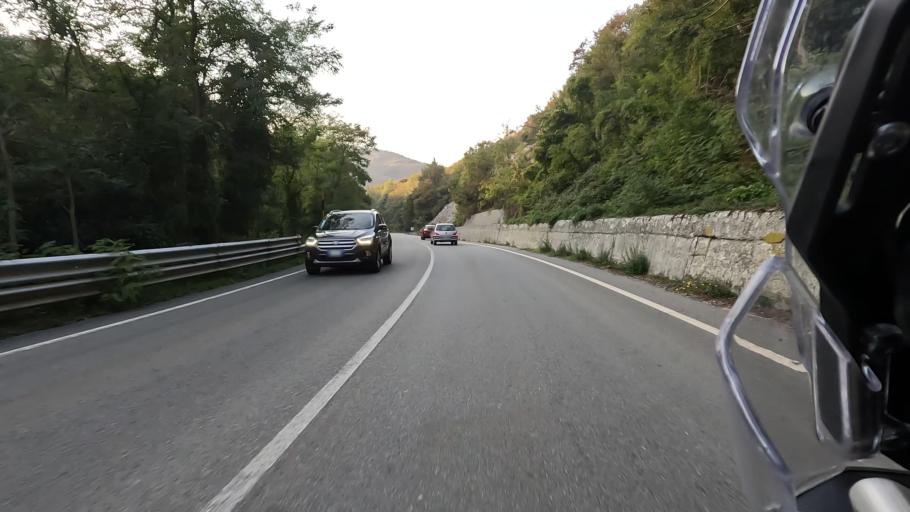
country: IT
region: Liguria
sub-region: Provincia di Savona
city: Osteria dei Cacciatori-Stella
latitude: 44.4438
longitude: 8.4841
